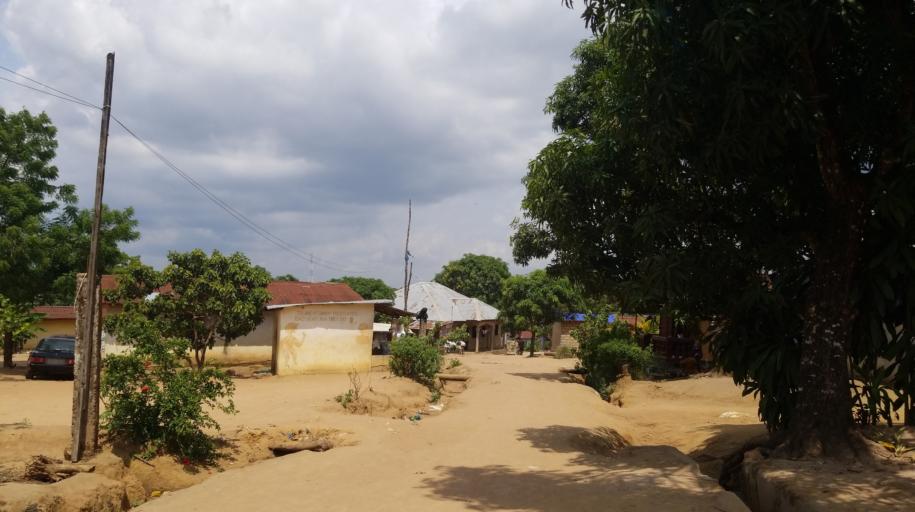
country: SL
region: Western Area
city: Waterloo
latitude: 8.3197
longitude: -13.0534
